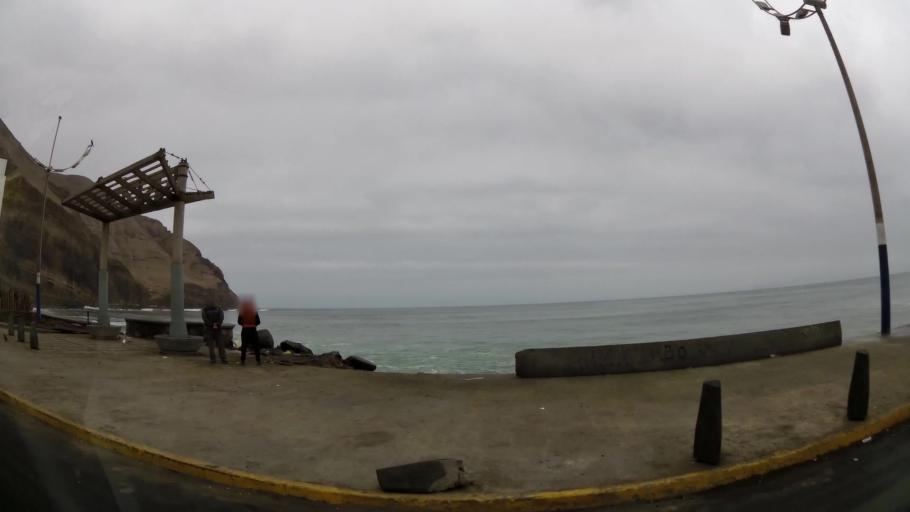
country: PE
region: Lima
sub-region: Lima
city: Surco
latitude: -12.1758
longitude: -77.0333
